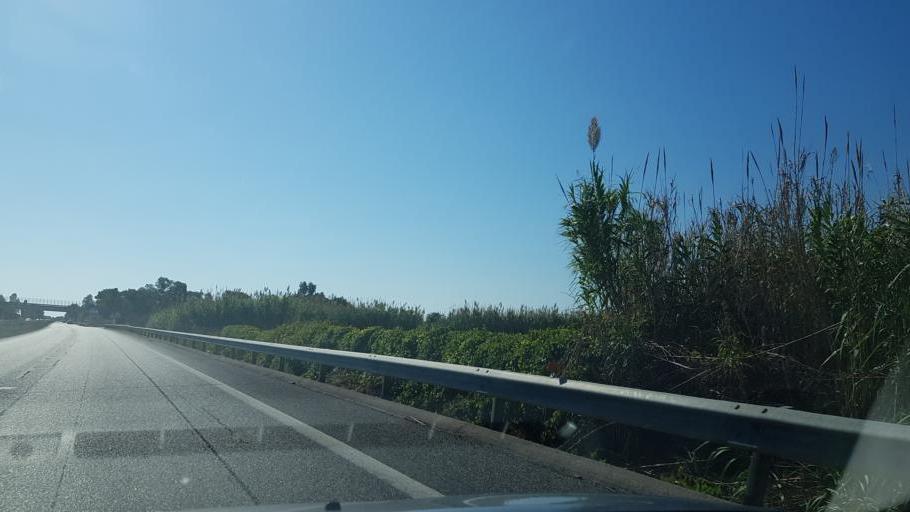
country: IT
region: Apulia
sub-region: Provincia di Brindisi
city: San Pietro Vernotico
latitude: 40.5241
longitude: 18.0145
